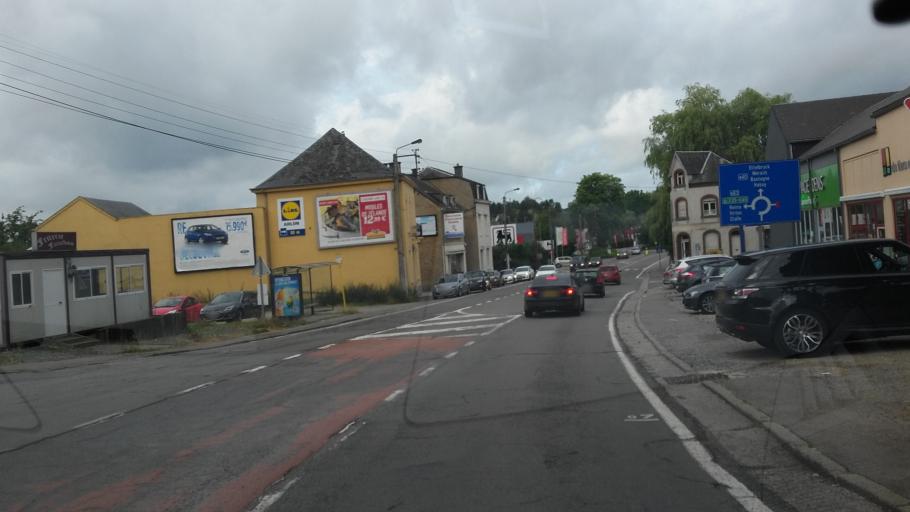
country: BE
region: Wallonia
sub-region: Province du Luxembourg
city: Arlon
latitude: 49.6855
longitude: 5.8004
